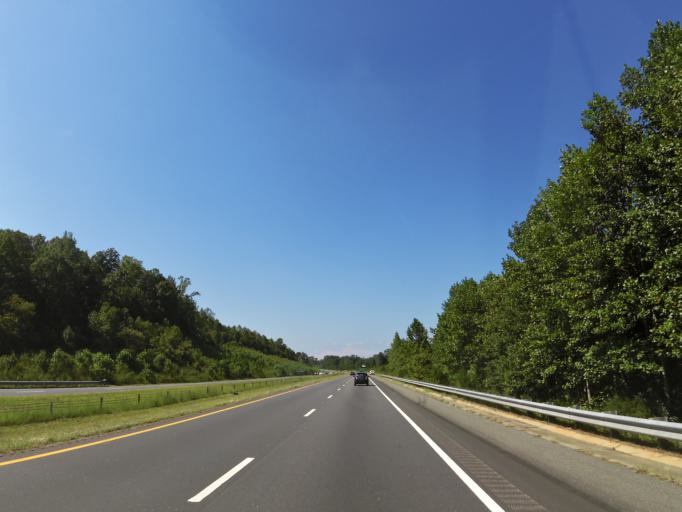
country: US
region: North Carolina
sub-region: Catawba County
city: Newton
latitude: 35.6220
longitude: -81.2890
